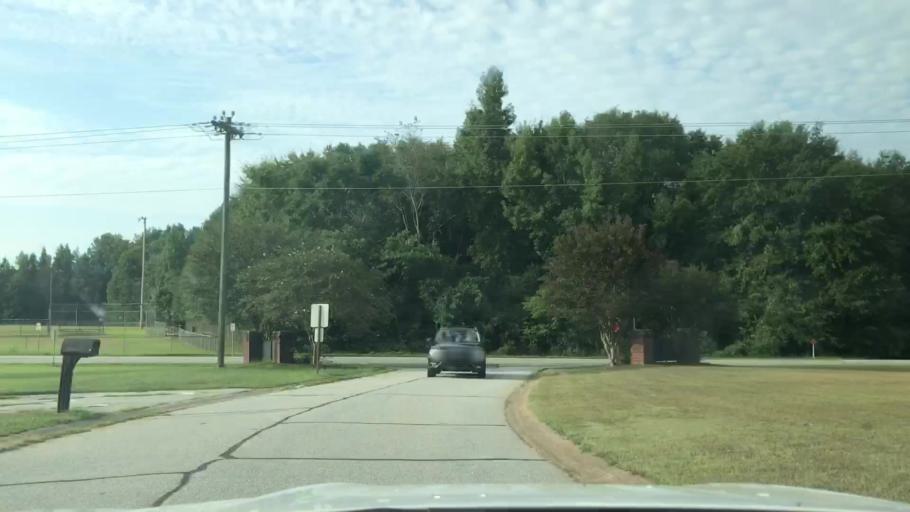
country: US
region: South Carolina
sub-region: Spartanburg County
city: Roebuck
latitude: 34.7961
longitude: -81.9178
